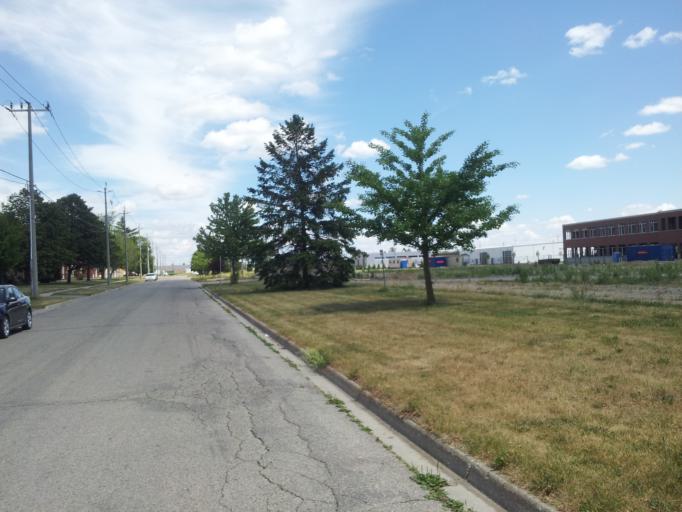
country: CA
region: Ontario
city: Stratford
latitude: 43.3685
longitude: -80.9624
